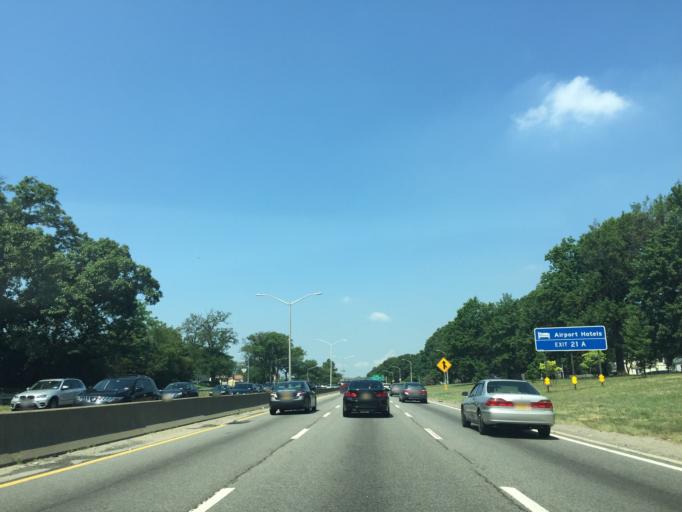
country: US
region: New York
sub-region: Nassau County
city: South Valley Stream
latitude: 40.6666
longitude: -73.7628
